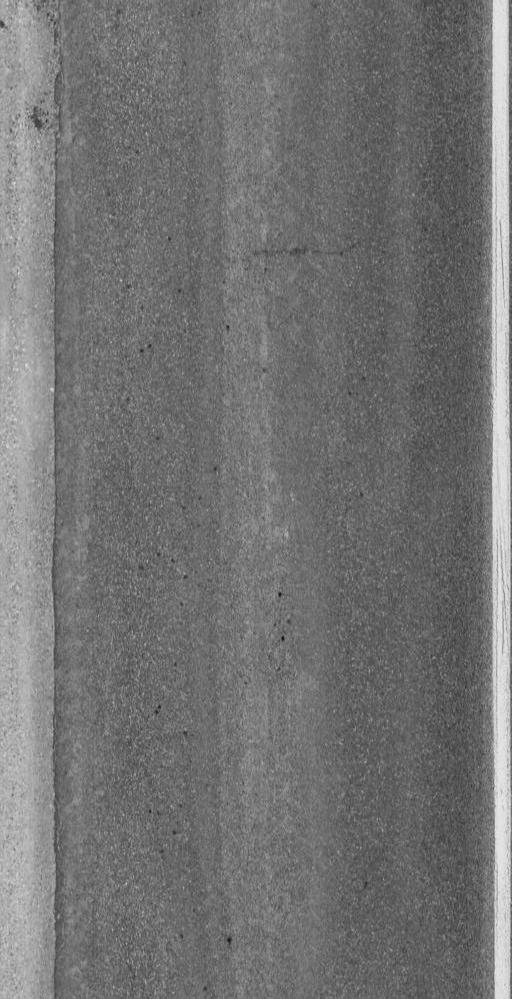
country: US
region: Vermont
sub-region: Chittenden County
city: South Burlington
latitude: 44.3989
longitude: -73.1768
